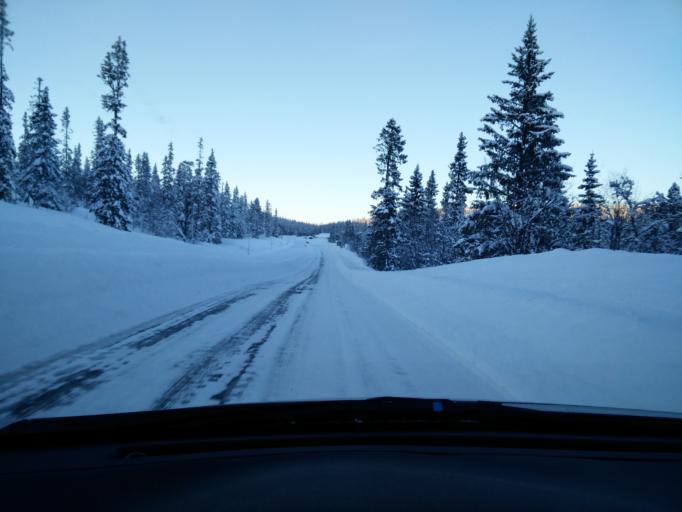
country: SE
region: Jaemtland
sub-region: Bergs Kommun
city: Hoverberg
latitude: 62.4980
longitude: 14.1110
